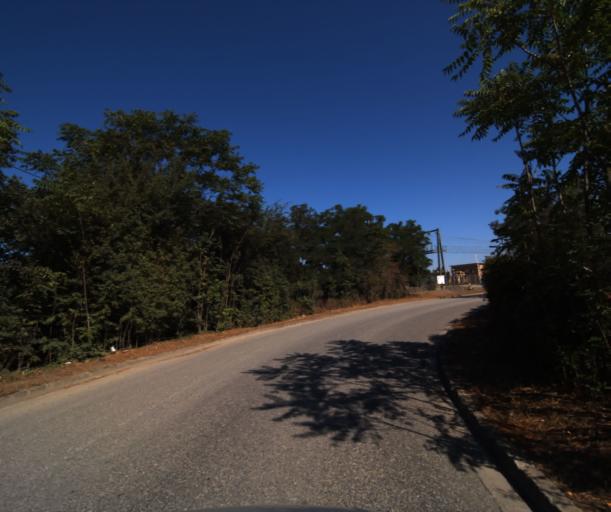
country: FR
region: Midi-Pyrenees
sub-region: Departement de la Haute-Garonne
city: Saubens
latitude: 43.4861
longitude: 1.3344
